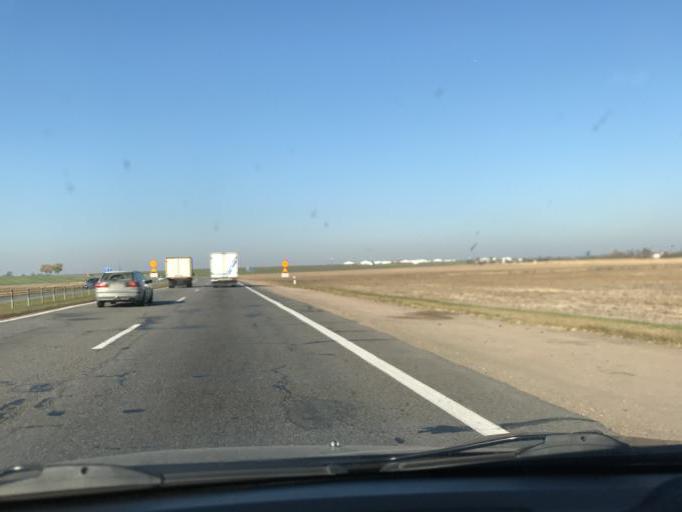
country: BY
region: Minsk
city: Dukora
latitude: 53.6720
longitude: 27.9340
